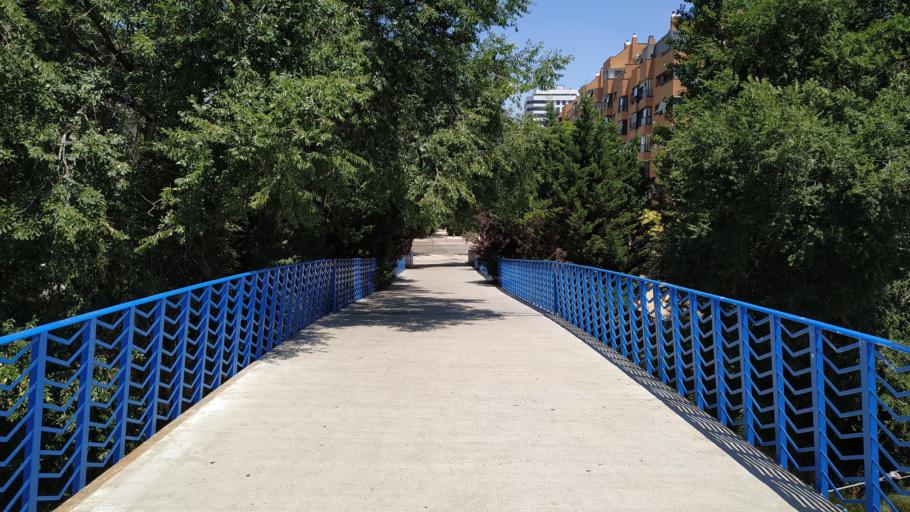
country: ES
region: Madrid
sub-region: Provincia de Madrid
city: Arganzuela
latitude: 40.3976
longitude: -3.6869
